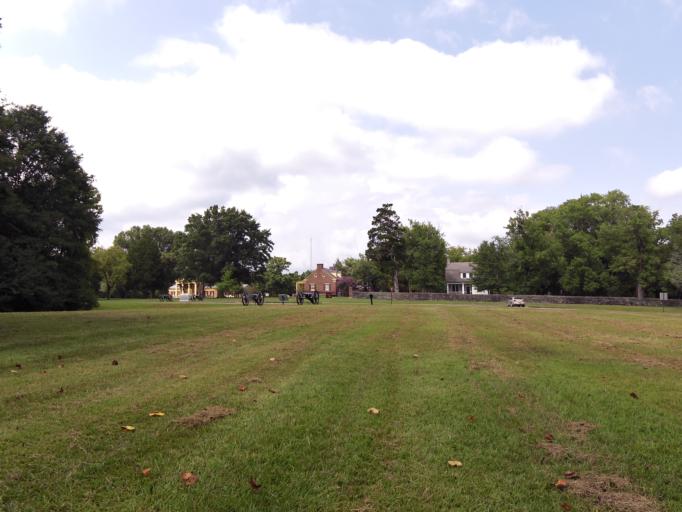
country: US
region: Tennessee
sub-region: Hardin County
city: Crump
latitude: 35.1497
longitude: -88.3212
